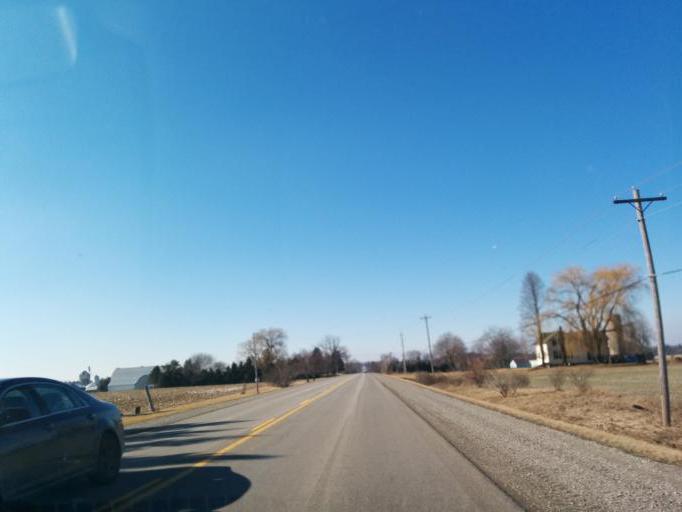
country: CA
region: Ontario
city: Brant
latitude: 43.0298
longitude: -80.3454
